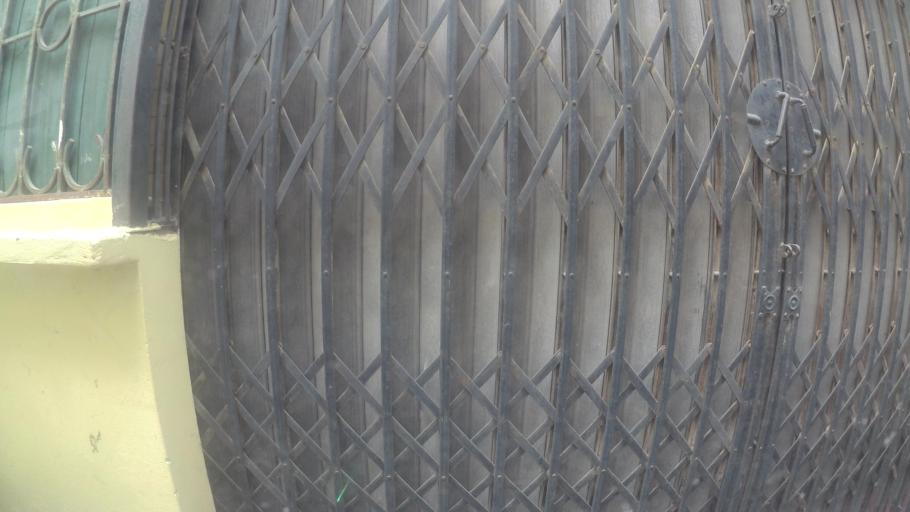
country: VN
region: Ha Noi
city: Tay Ho
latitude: 21.0623
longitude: 105.8347
